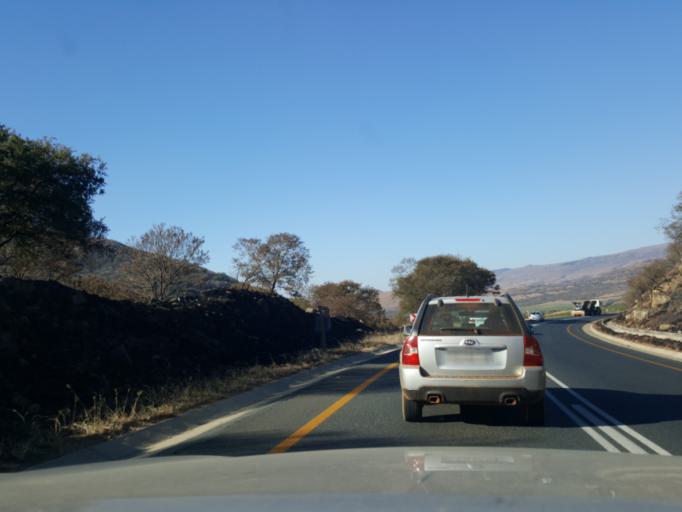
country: ZA
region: Mpumalanga
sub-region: Ehlanzeni District
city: Lydenburg
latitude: -25.4407
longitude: 30.4330
